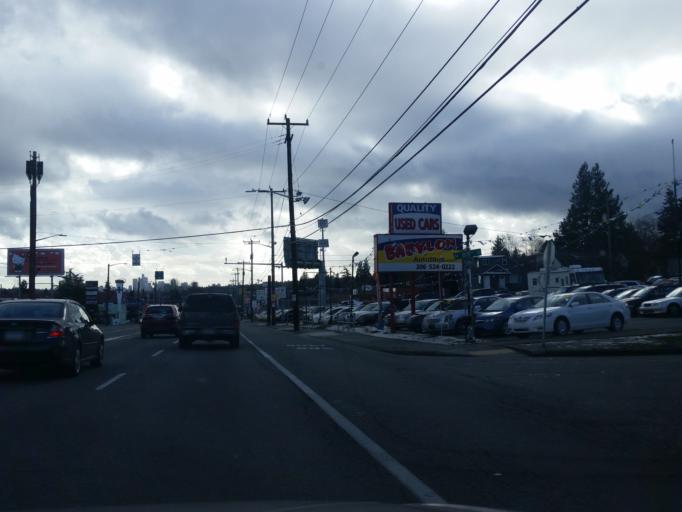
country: US
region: Washington
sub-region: King County
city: Shoreline
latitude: 47.6929
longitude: -122.3446
